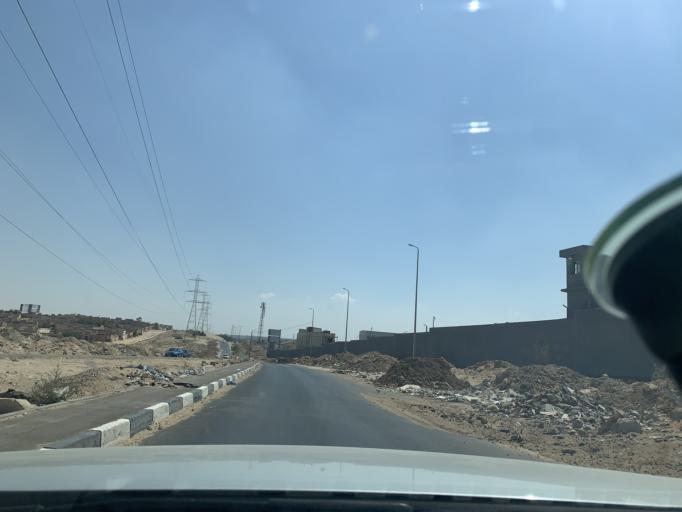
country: EG
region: Muhafazat al Qahirah
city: Cairo
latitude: 30.0280
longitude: 31.3474
